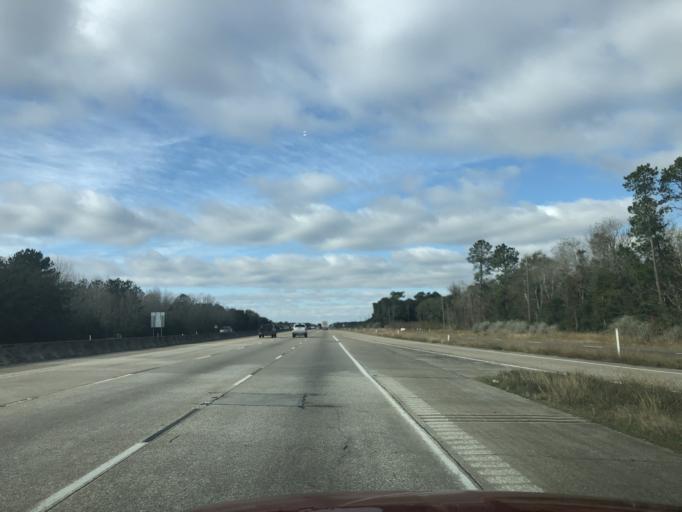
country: US
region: Texas
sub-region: Chambers County
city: Anahuac
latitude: 29.8378
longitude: -94.5831
